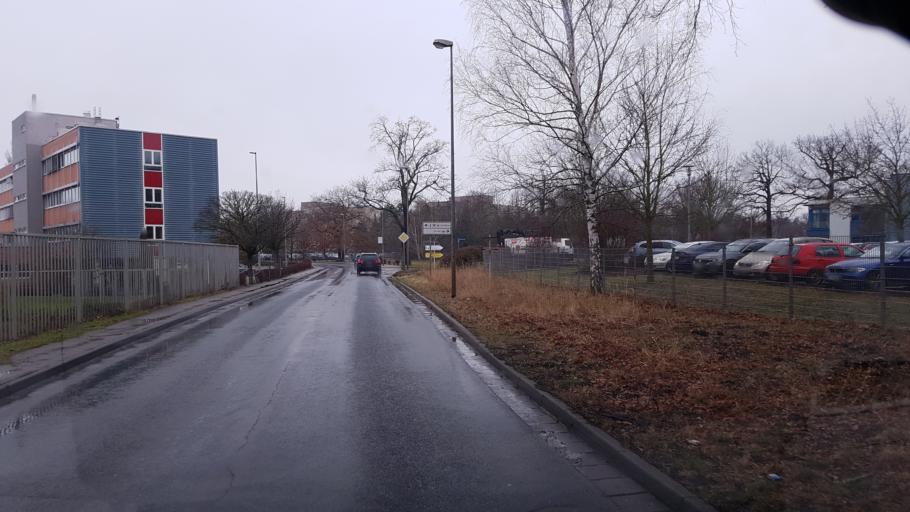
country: DE
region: Brandenburg
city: Lauchhammer
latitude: 51.4986
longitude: 13.8028
